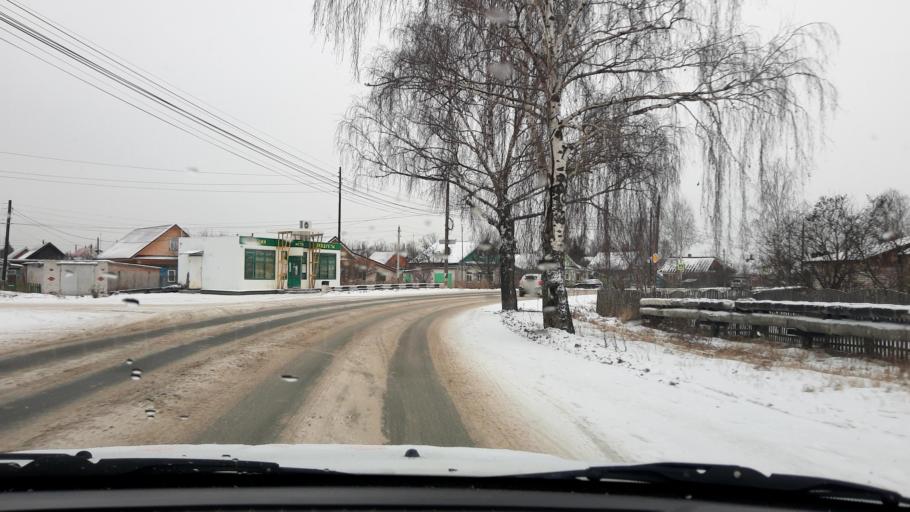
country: RU
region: Nizjnij Novgorod
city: Gorodets
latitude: 56.6477
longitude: 43.4897
